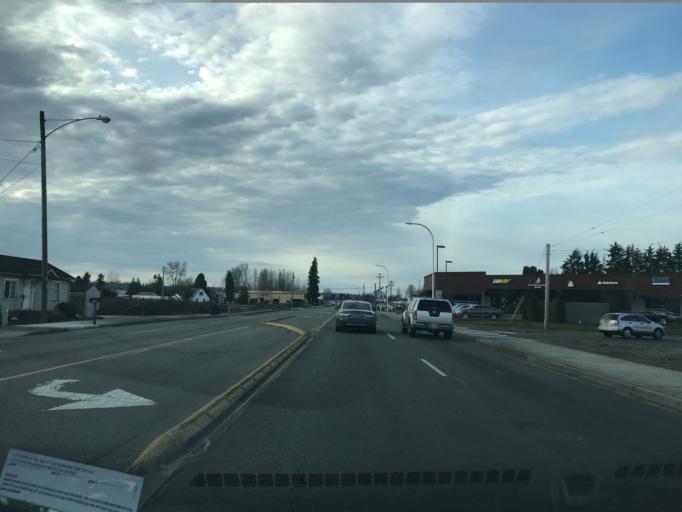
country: US
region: Washington
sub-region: King County
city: Kent
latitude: 47.3495
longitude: -122.2252
